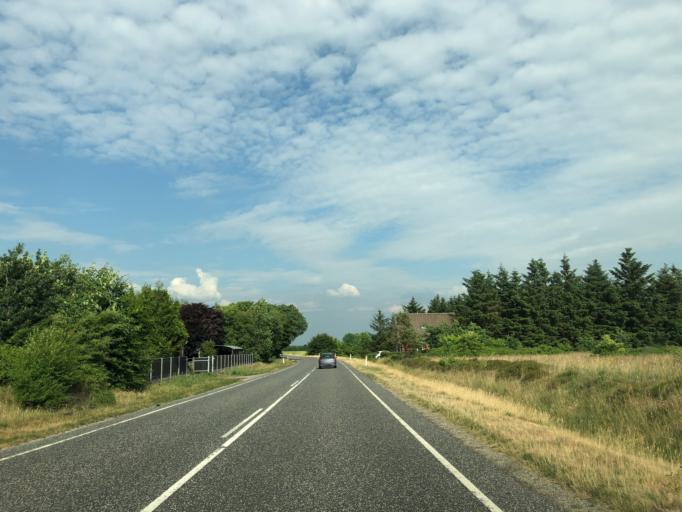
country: DK
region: Central Jutland
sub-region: Ringkobing-Skjern Kommune
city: Skjern
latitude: 55.9000
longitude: 8.4740
